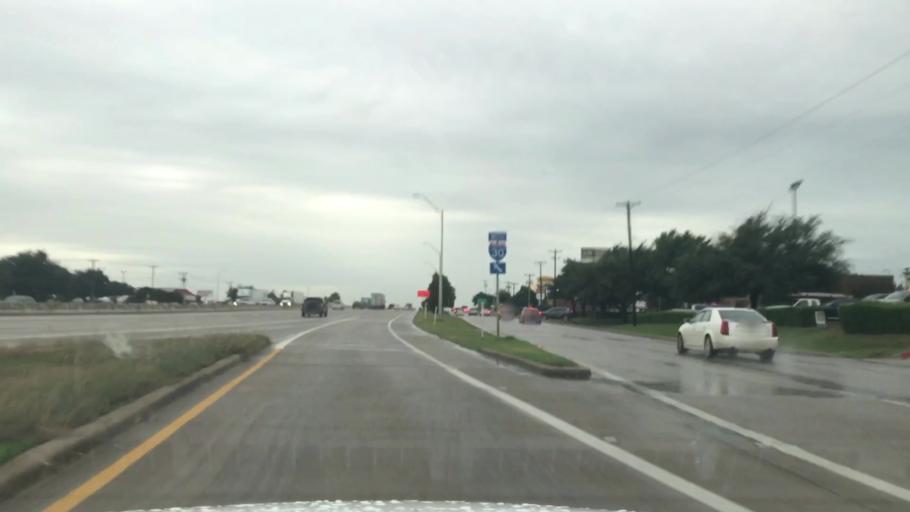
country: US
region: Texas
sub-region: Rockwall County
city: Rockwall
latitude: 32.8989
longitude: -96.4648
